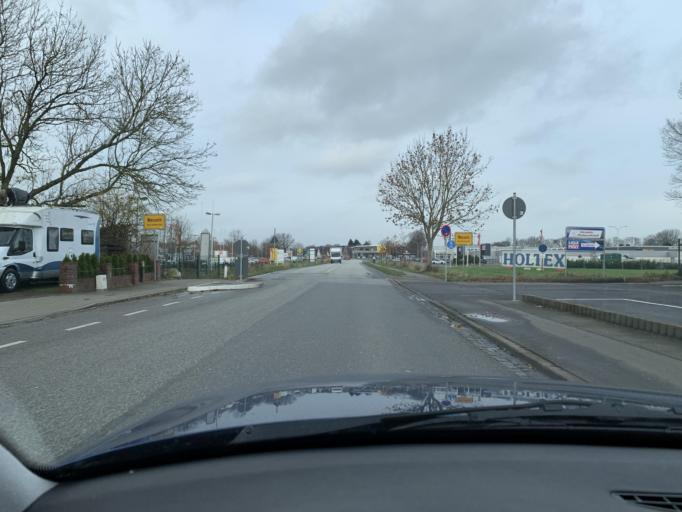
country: DE
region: Schleswig-Holstein
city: Wesseln
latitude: 54.2047
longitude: 9.0885
